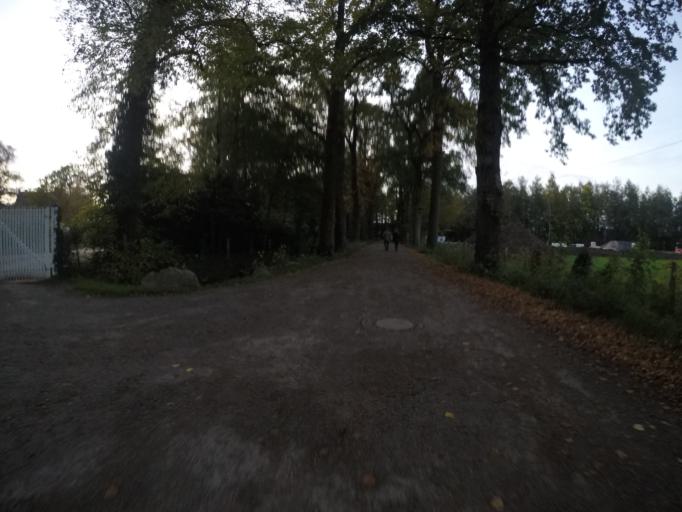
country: DE
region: North Rhine-Westphalia
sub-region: Regierungsbezirk Munster
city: Rhede
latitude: 51.8412
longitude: 6.7032
